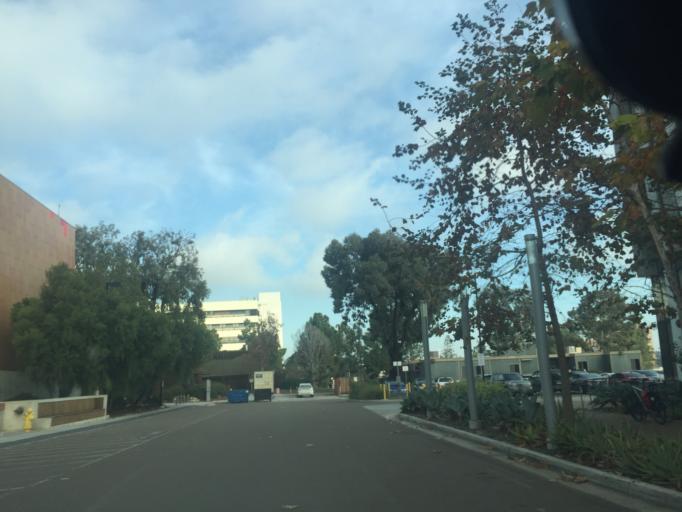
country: US
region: California
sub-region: San Diego County
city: La Jolla
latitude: 32.8748
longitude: -117.2350
